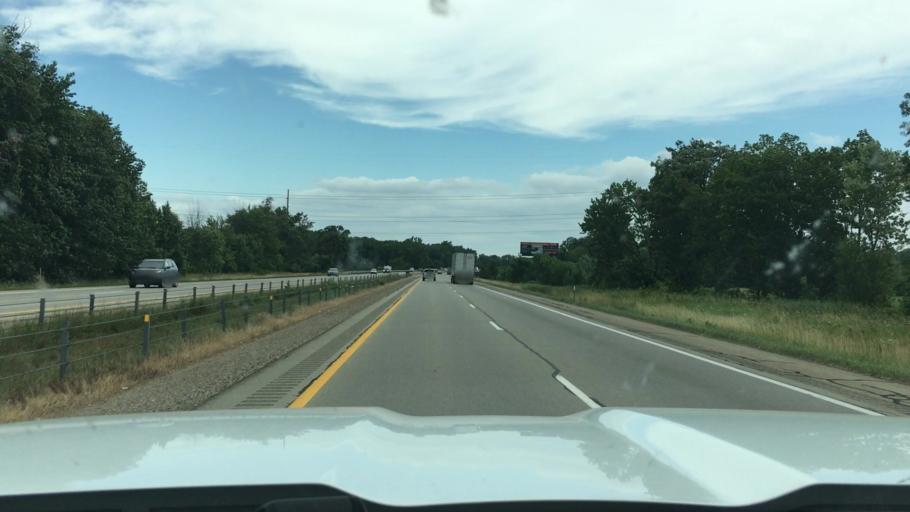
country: US
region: Michigan
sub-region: Kent County
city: Byron Center
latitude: 42.7570
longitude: -85.6735
